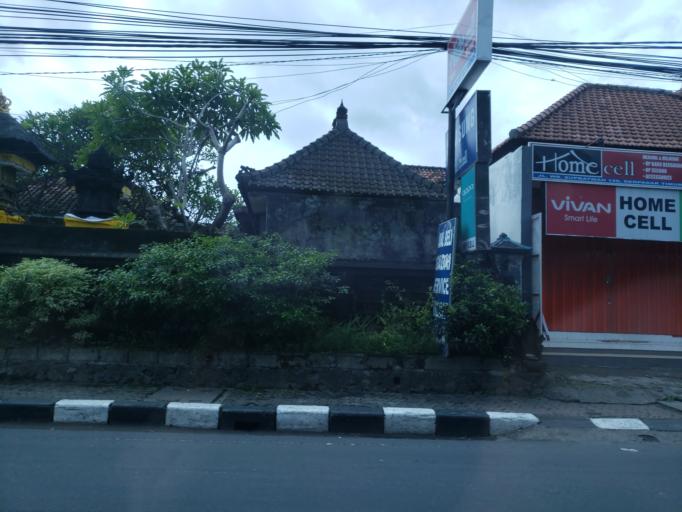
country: ID
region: Bali
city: Dajan Tangluk
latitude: -8.6482
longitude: 115.2394
